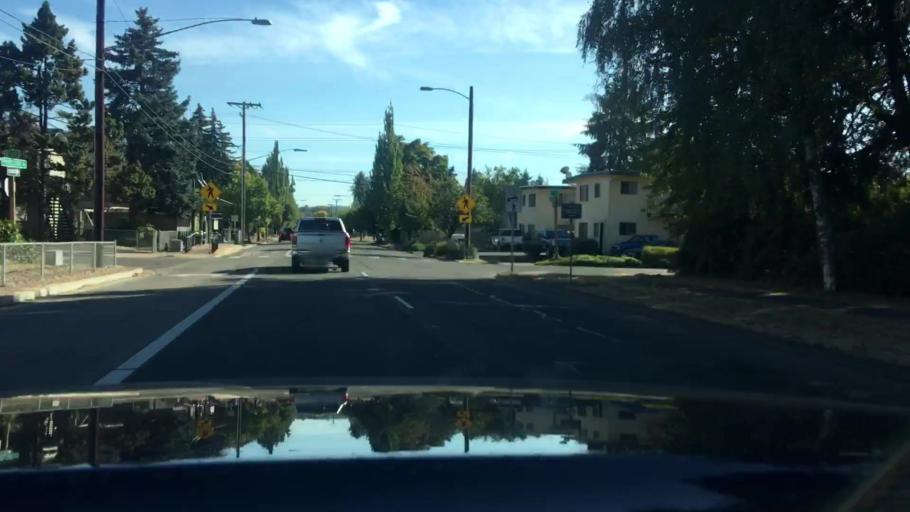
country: US
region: Oregon
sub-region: Lane County
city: Springfield
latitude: 44.0517
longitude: -123.0232
